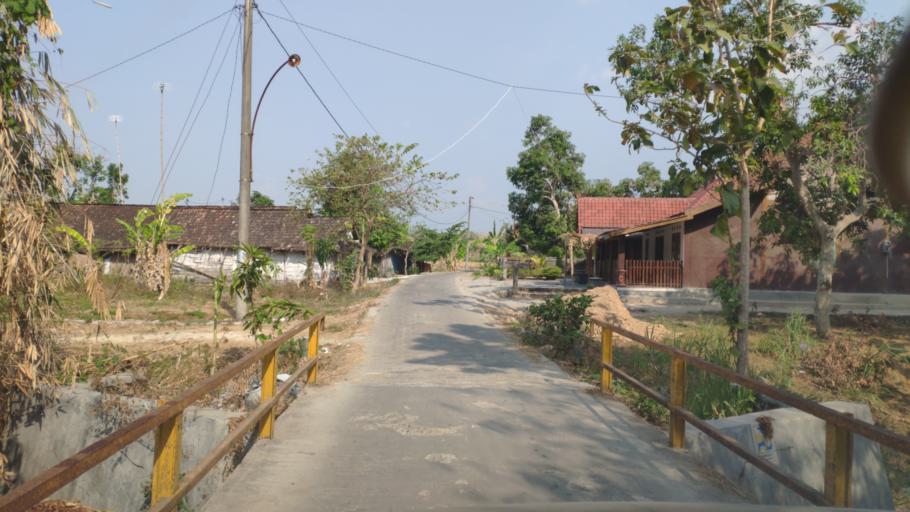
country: ID
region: Central Java
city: Jomblang
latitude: -7.0221
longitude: 111.4454
